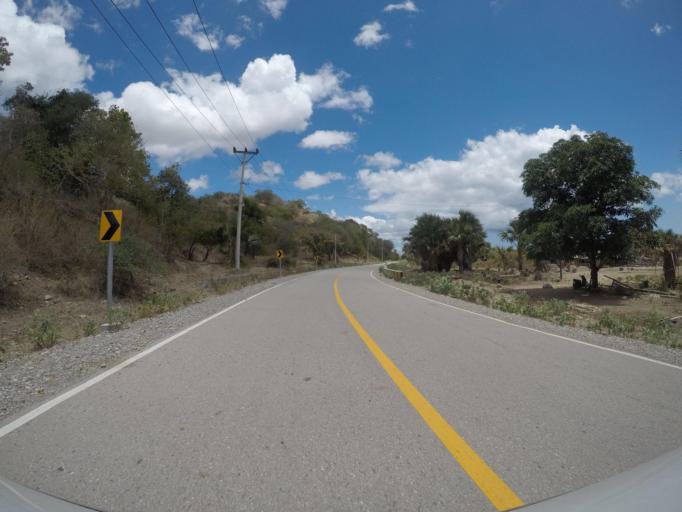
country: TL
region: Lautem
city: Lospalos
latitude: -8.4152
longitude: 126.8036
